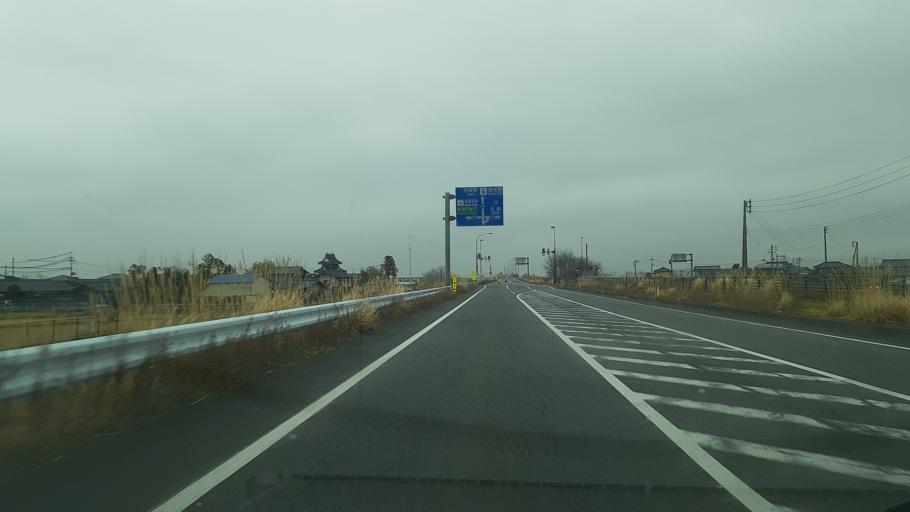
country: JP
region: Niigata
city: Kameda-honcho
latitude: 37.8749
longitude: 139.1567
